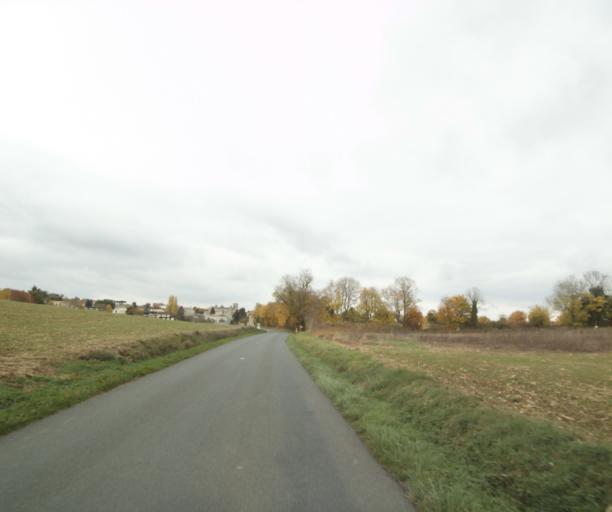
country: FR
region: Poitou-Charentes
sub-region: Departement de la Charente-Maritime
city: Bussac-sur-Charente
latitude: 45.7794
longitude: -0.6733
